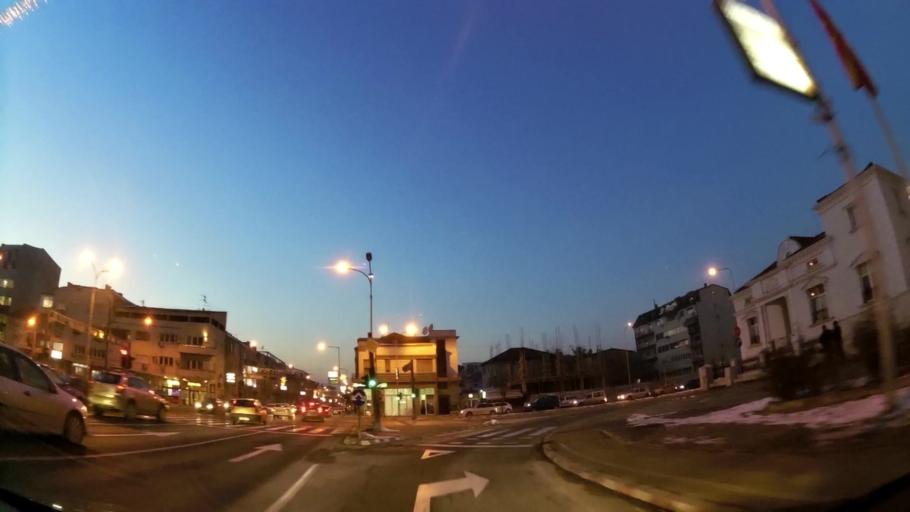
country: MK
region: Karpos
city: Skopje
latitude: 42.0003
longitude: 21.4276
